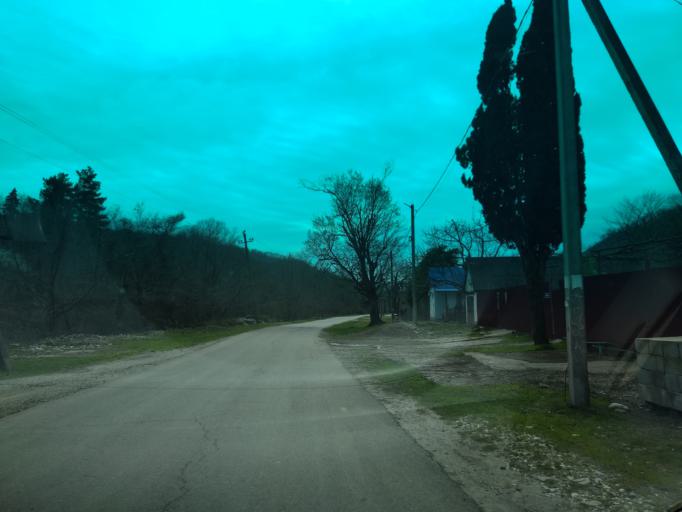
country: RU
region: Krasnodarskiy
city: Shepsi
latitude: 44.0616
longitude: 39.1368
